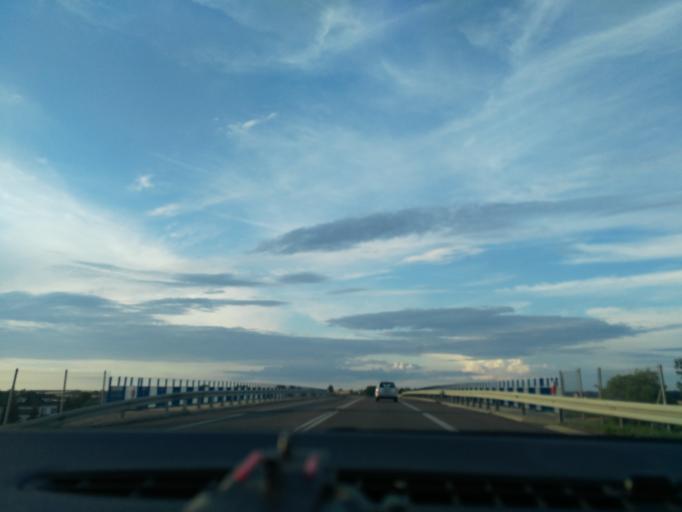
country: PL
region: Lublin Voivodeship
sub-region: Powiat lubelski
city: Niedrzwica Duza
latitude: 51.1271
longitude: 22.3926
